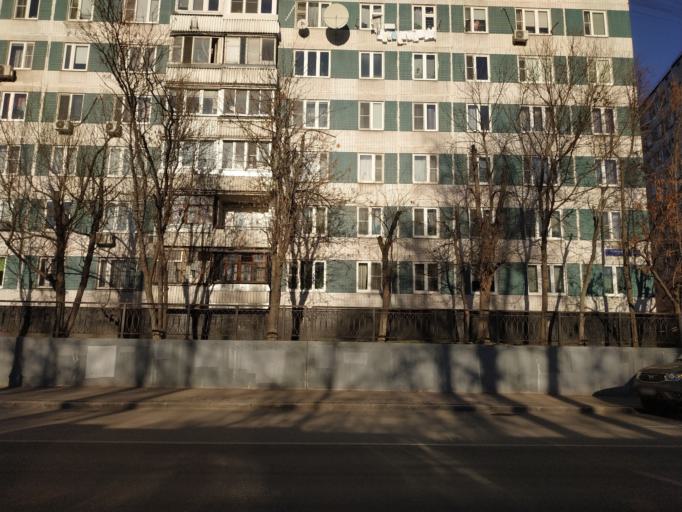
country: RU
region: Moscow
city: Biryulevo
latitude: 55.5774
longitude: 37.6817
